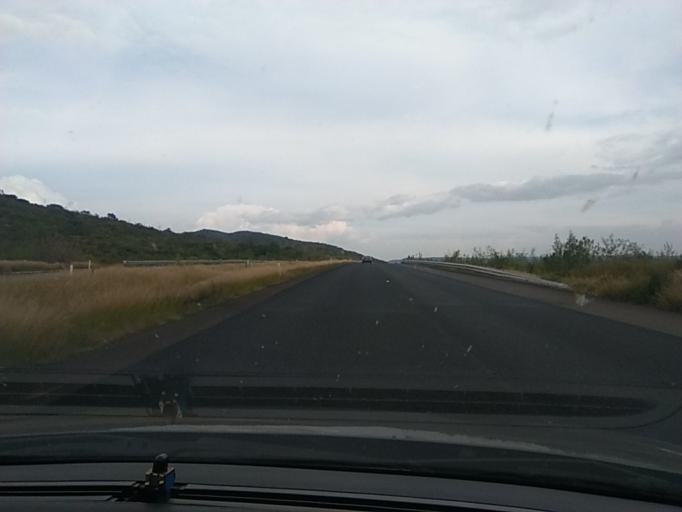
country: MX
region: Mexico
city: Huaniqueo de Morales
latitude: 19.8839
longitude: -101.4298
